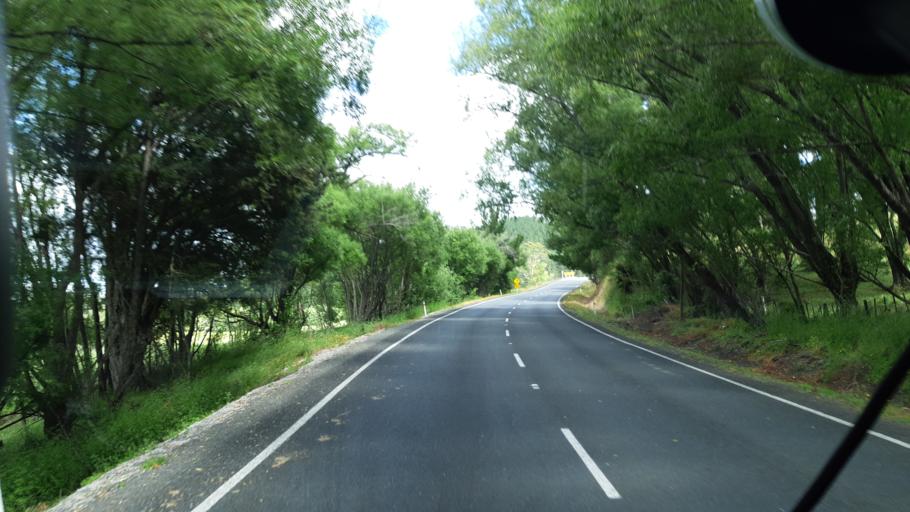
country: NZ
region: Northland
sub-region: Far North District
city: Taipa
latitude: -35.2545
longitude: 173.5552
